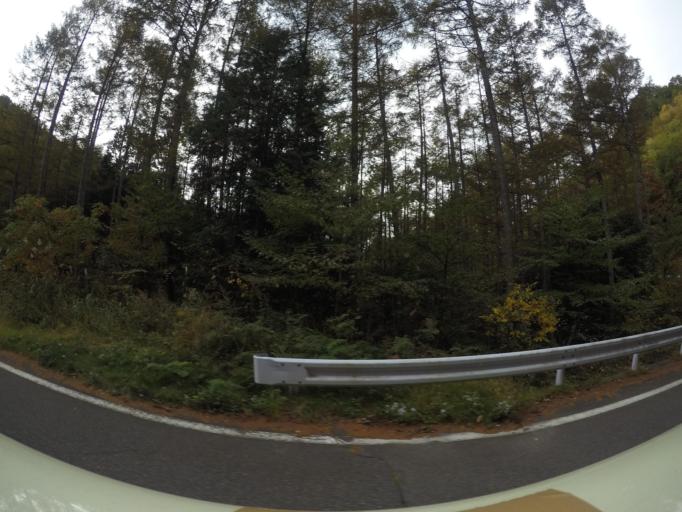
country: JP
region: Nagano
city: Ina
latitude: 35.9379
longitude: 137.5906
